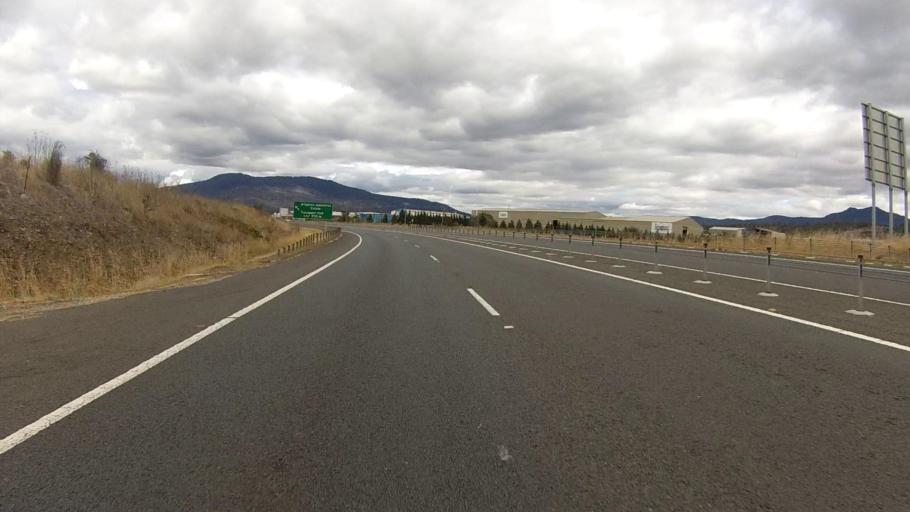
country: AU
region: Tasmania
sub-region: Brighton
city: Bridgewater
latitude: -42.7170
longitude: 147.2400
